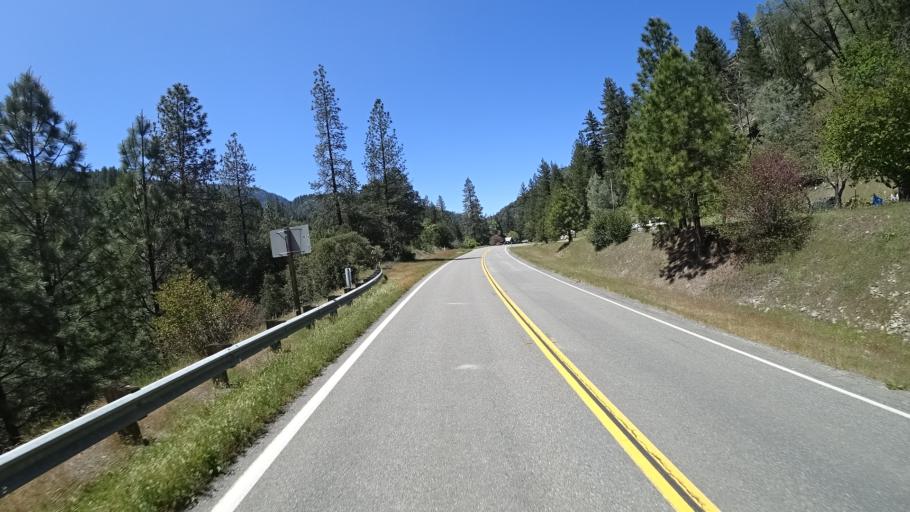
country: US
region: California
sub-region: Trinity County
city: Hayfork
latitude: 40.7425
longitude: -123.2665
